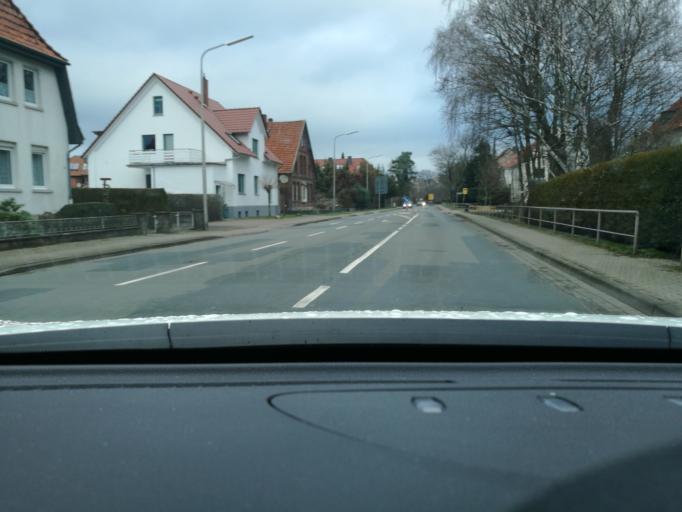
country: DE
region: Lower Saxony
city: Stadthagen
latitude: 52.3166
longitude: 9.2028
